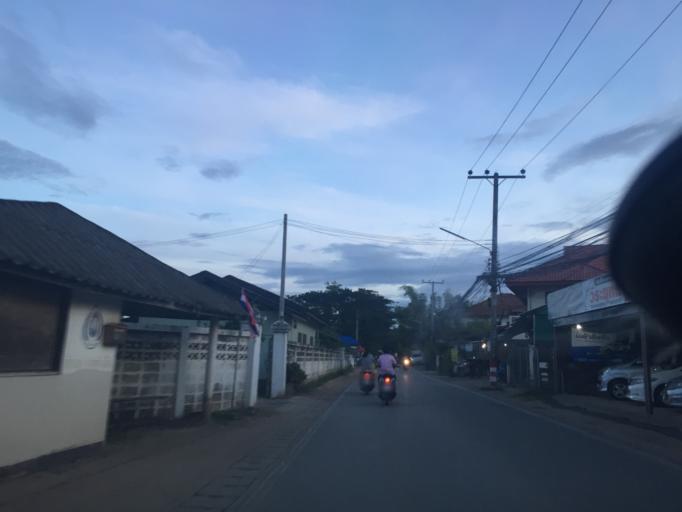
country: TH
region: Lamphun
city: Lamphun
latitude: 18.5560
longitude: 99.0358
